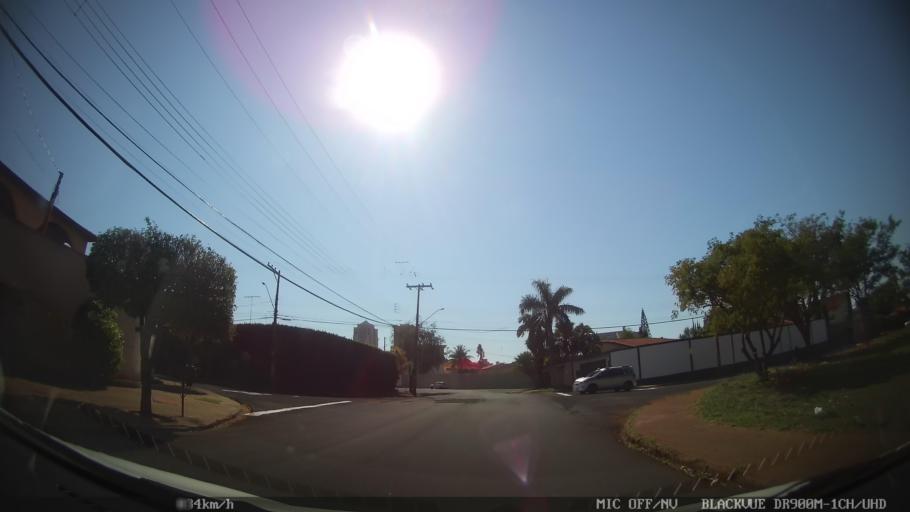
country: BR
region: Sao Paulo
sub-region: Ribeirao Preto
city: Ribeirao Preto
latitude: -21.2041
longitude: -47.7721
